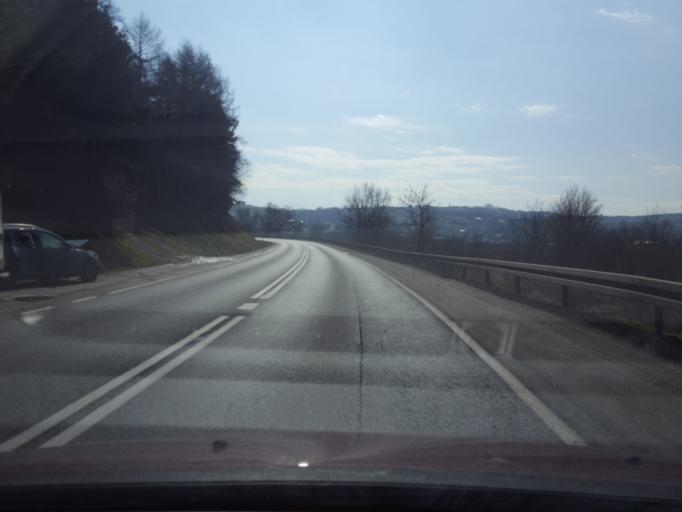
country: PL
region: Lesser Poland Voivodeship
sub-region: Powiat nowosadecki
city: Chelmiec
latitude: 49.6783
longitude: 20.6537
